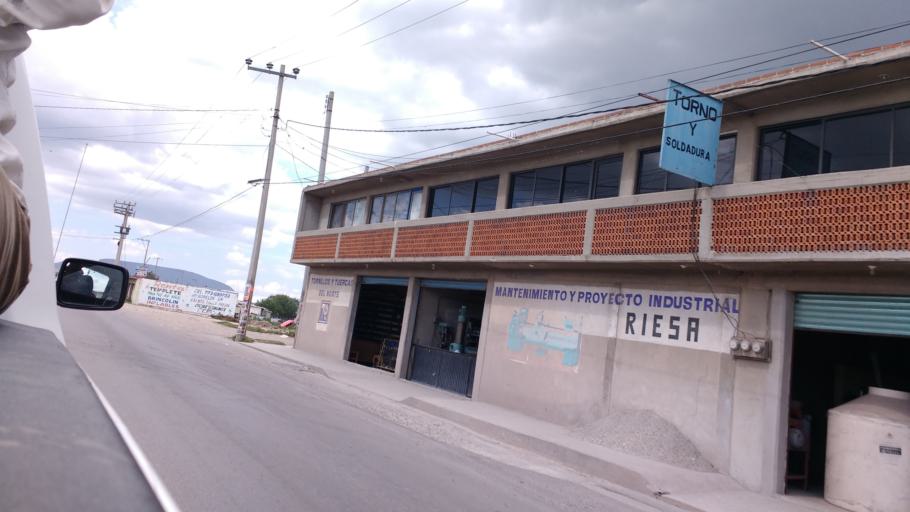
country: MX
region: Hidalgo
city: Tlahuelilpan
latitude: 20.1448
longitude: -99.2351
